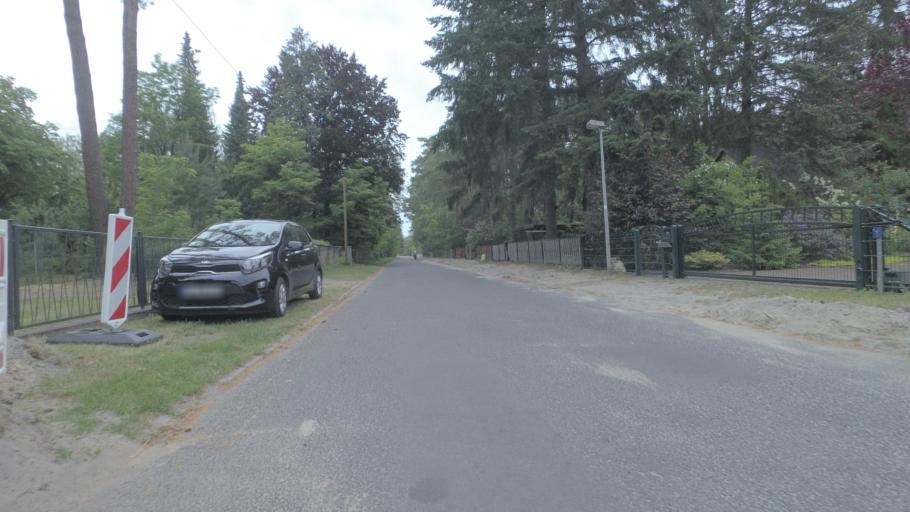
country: DE
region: Brandenburg
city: Bestensee
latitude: 52.2693
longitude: 13.7585
